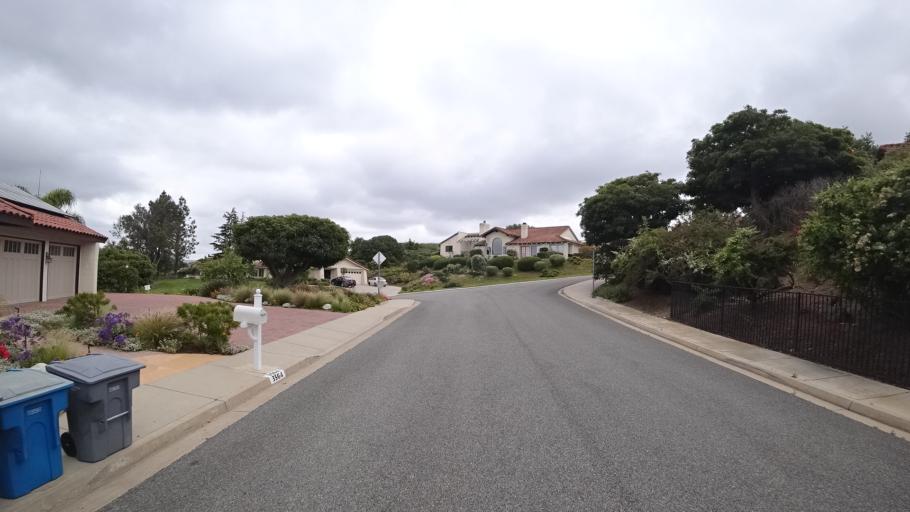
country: US
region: California
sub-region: Ventura County
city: Casa Conejo
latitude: 34.2269
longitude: -118.9015
